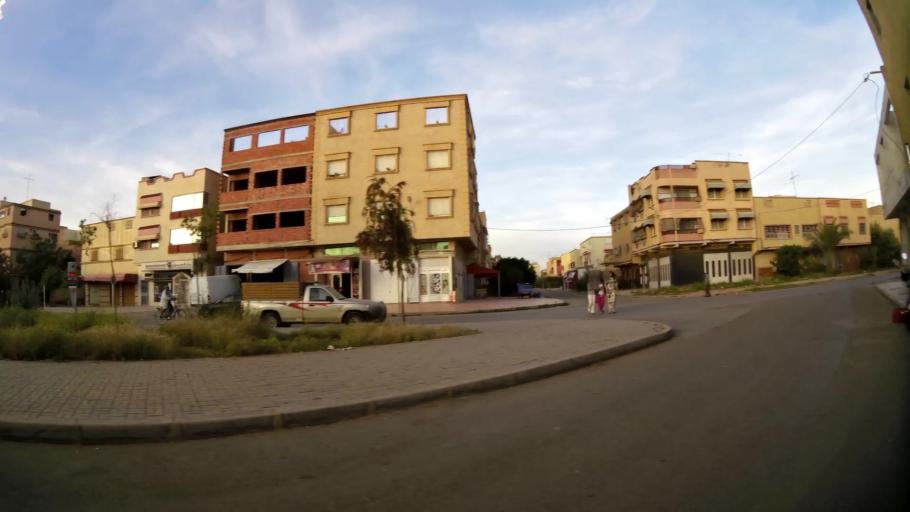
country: MA
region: Oriental
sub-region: Oujda-Angad
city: Oujda
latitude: 34.6789
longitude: -1.8829
